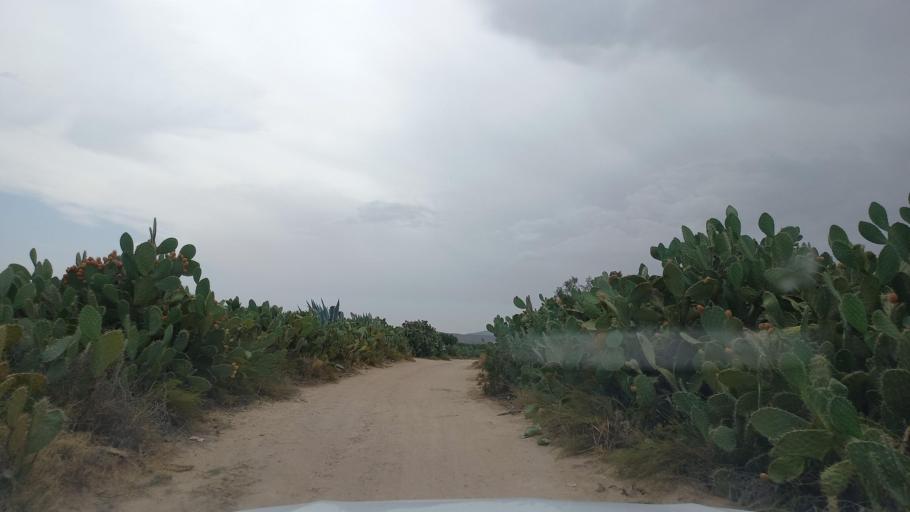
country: TN
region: Al Qasrayn
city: Kasserine
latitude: 35.2378
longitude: 9.0175
